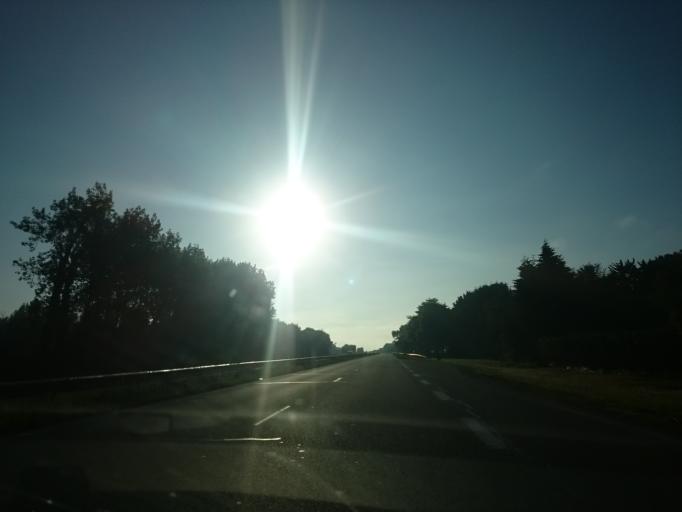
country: FR
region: Brittany
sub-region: Departement du Finistere
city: Gouesnou
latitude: 48.4332
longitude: -4.4614
